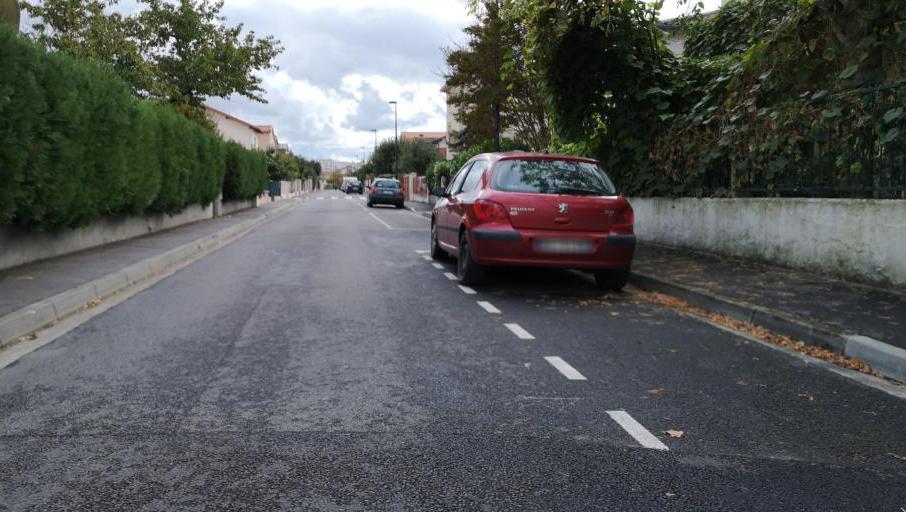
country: FR
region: Midi-Pyrenees
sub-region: Departement de la Haute-Garonne
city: Blagnac
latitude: 43.6080
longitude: 1.4114
